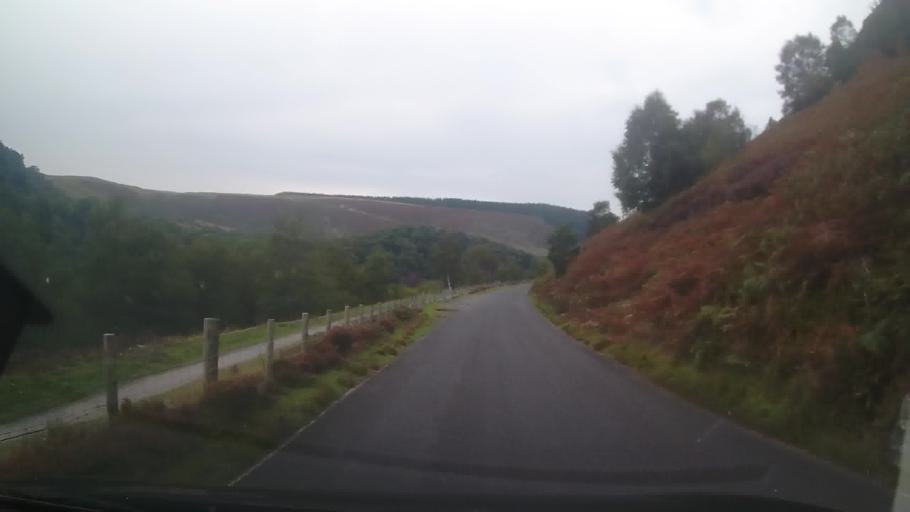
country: GB
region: Wales
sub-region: Sir Powys
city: Rhayader
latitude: 52.2748
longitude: -3.5925
